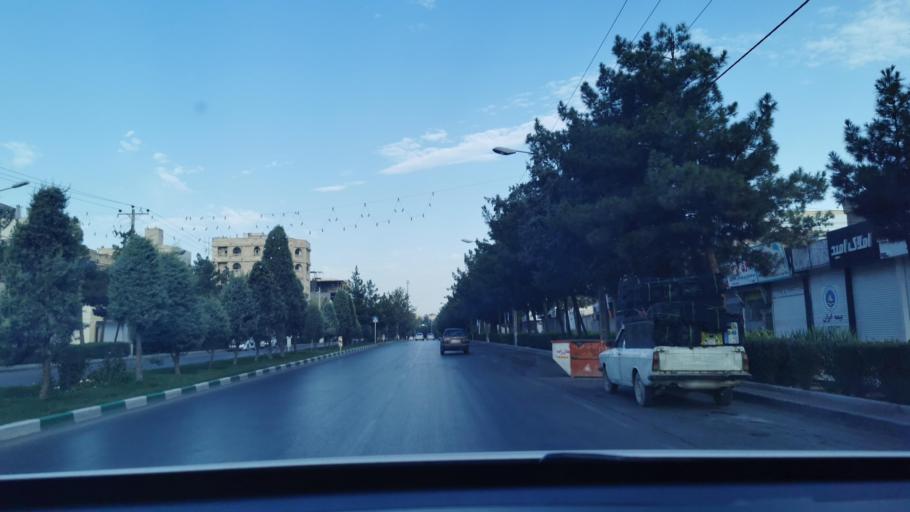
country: IR
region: Razavi Khorasan
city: Mashhad
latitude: 36.3594
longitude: 59.5110
